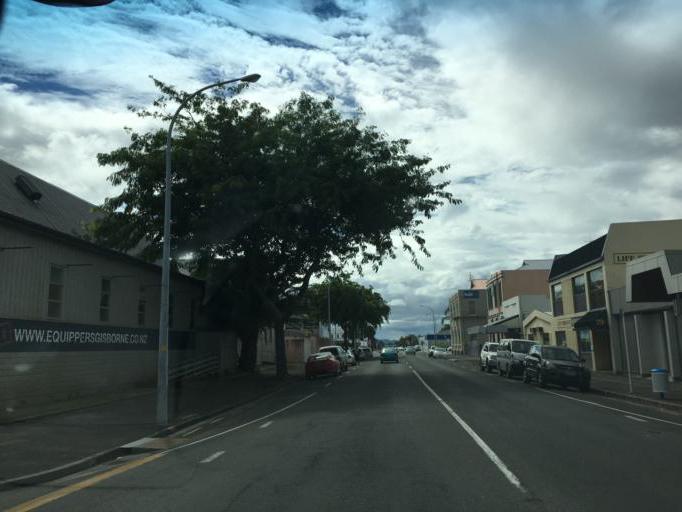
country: NZ
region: Gisborne
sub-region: Gisborne District
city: Gisborne
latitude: -38.6683
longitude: 178.0258
